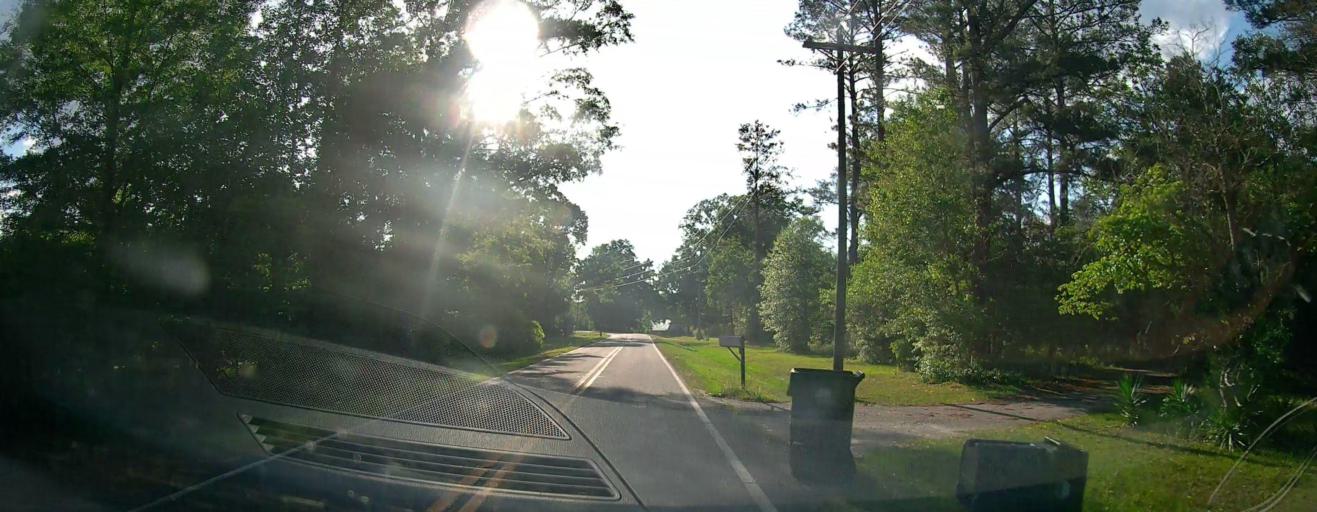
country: US
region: Georgia
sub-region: Peach County
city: Byron
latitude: 32.6718
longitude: -83.7947
